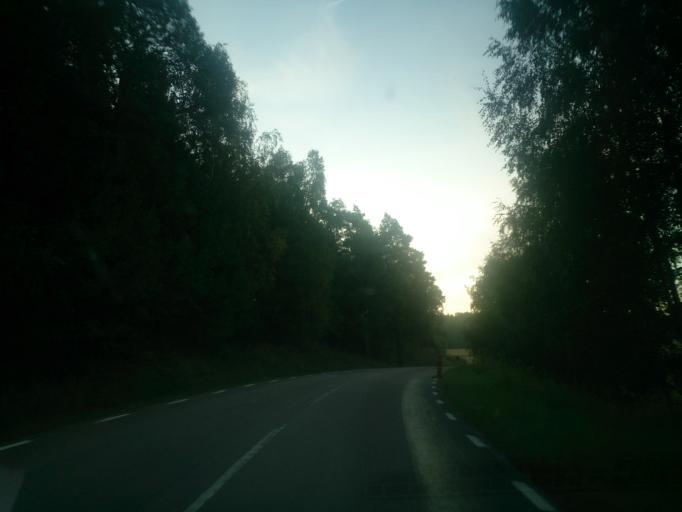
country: SE
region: Soedermanland
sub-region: Nykopings Kommun
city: Nykoping
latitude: 58.8671
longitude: 17.1768
